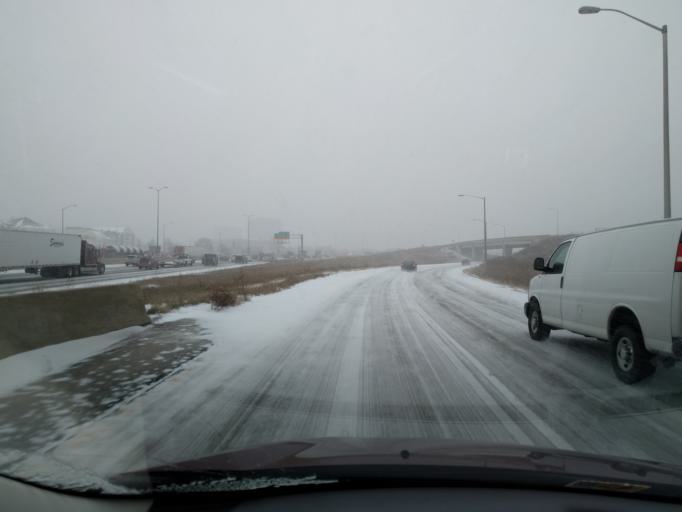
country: US
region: Wisconsin
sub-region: Waukesha County
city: Butler
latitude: 43.1557
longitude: -88.0584
